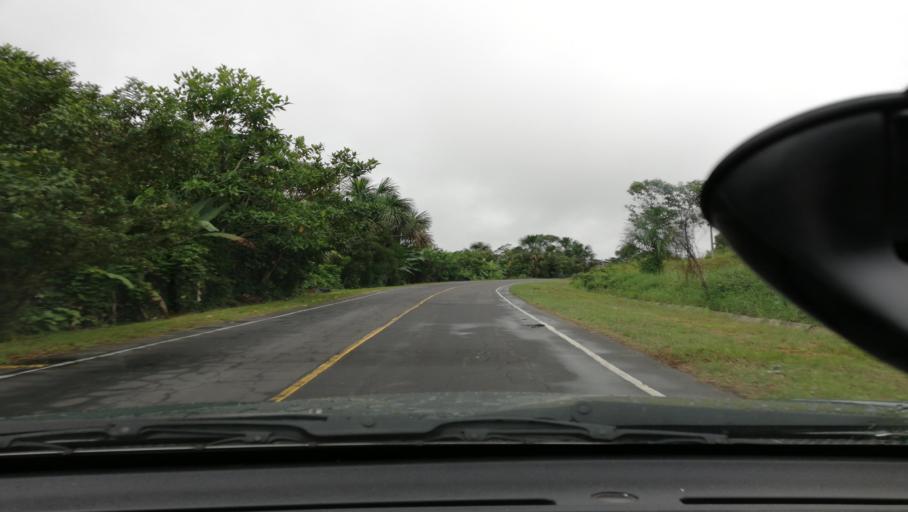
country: PE
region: Loreto
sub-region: Provincia de Maynas
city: San Juan
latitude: -4.0269
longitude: -73.4341
